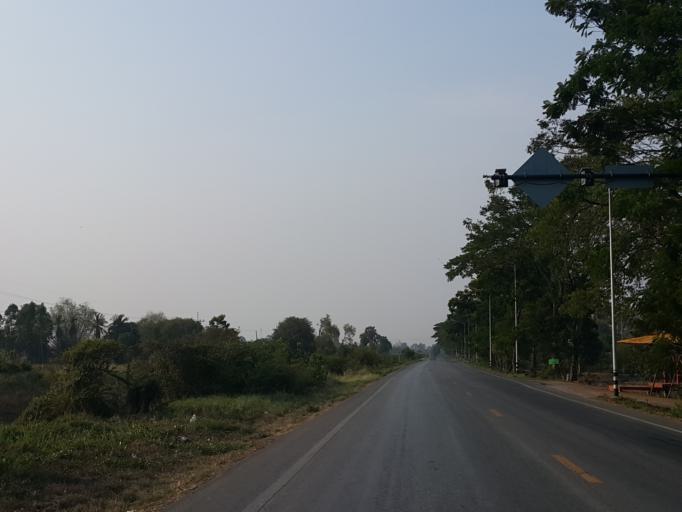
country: TH
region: Chai Nat
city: Sankhaburi
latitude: 15.0229
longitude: 100.1447
